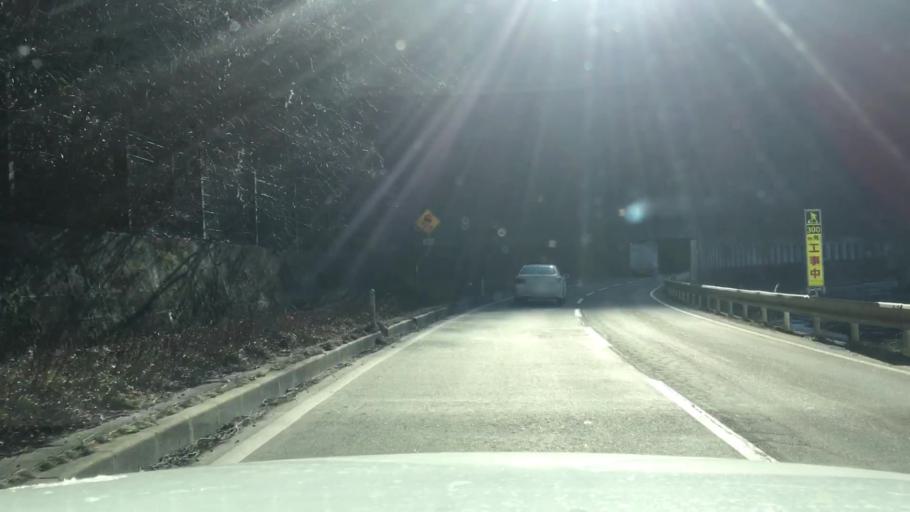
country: JP
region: Iwate
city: Miyako
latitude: 39.6074
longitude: 141.6527
